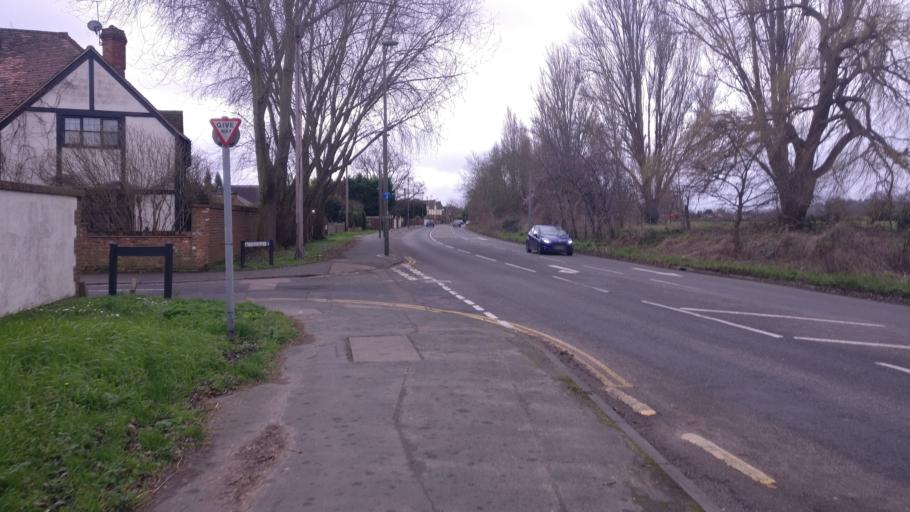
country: GB
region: England
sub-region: Surrey
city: Staines
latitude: 51.4287
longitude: -0.5131
